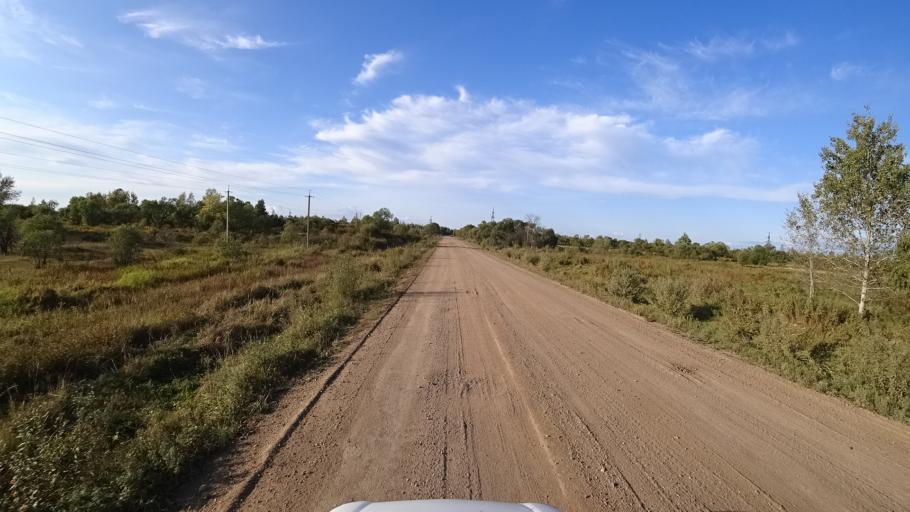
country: RU
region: Amur
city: Arkhara
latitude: 49.3630
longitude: 130.1365
